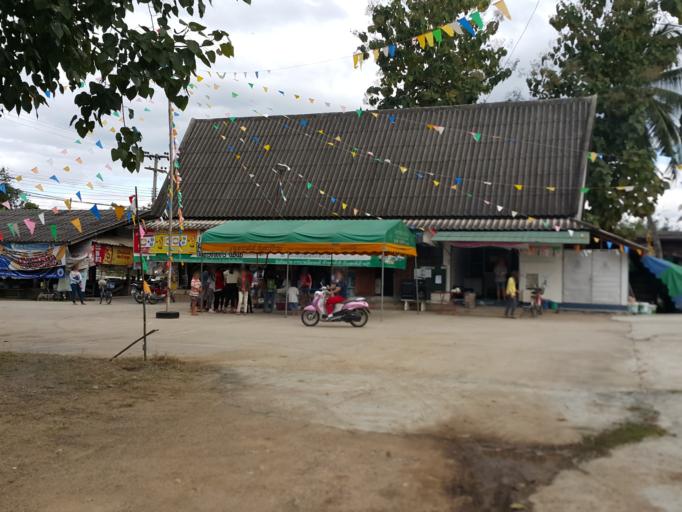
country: TH
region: Chiang Mai
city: San Sai
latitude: 18.8629
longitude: 99.1014
